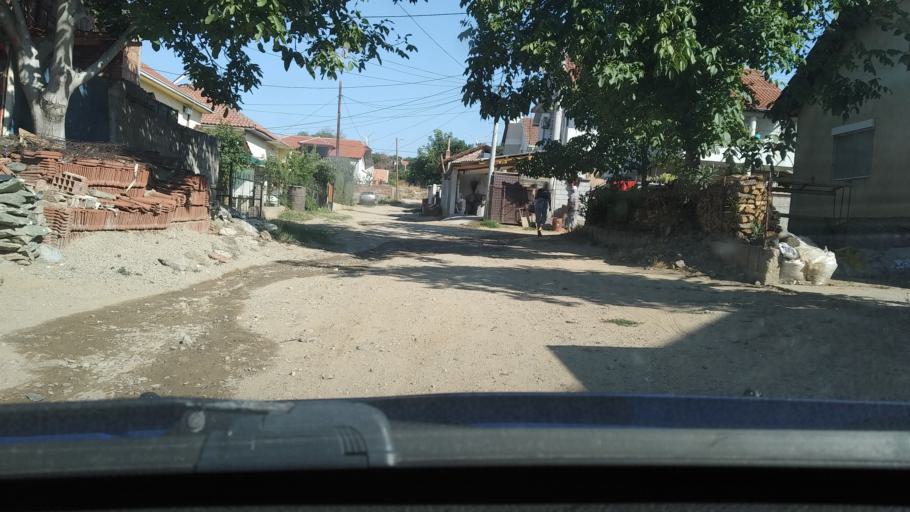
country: MK
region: Bogdanci
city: Bogdanci
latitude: 41.2048
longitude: 22.5675
